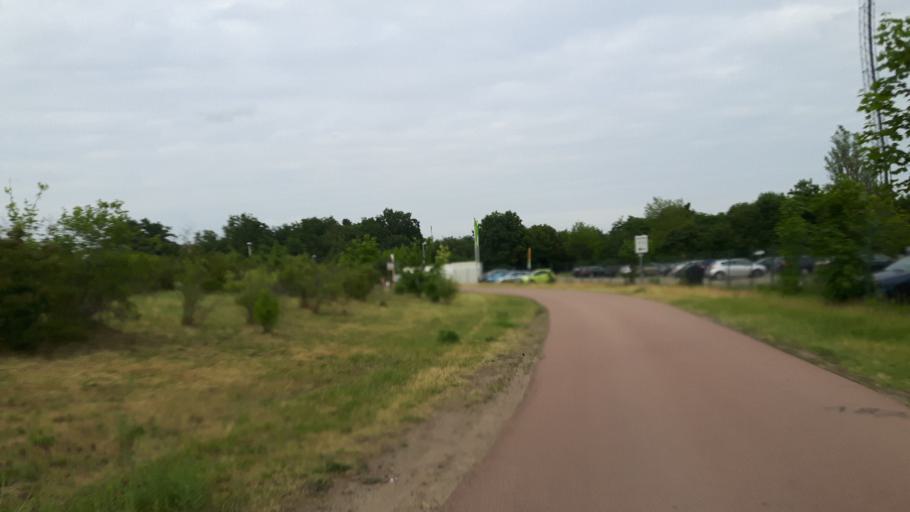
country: DE
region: Saxony-Anhalt
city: Wittenburg
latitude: 51.8625
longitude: 12.6569
